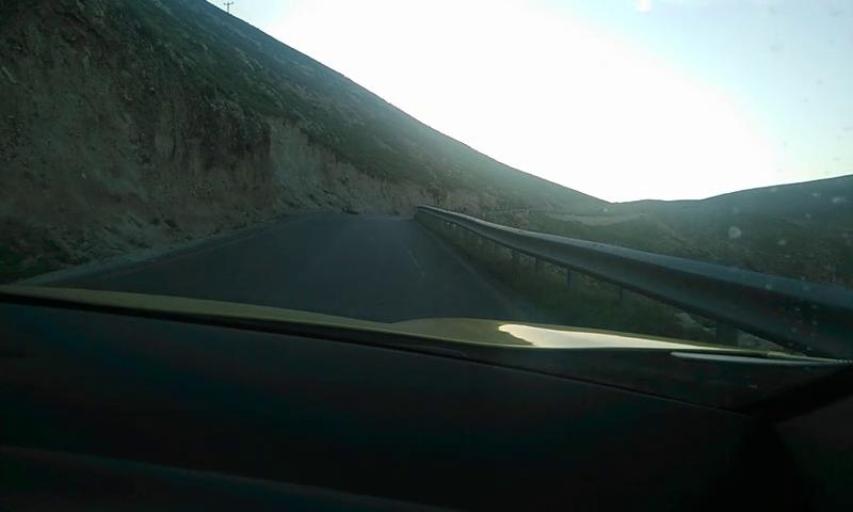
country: PS
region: West Bank
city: Rammun
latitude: 31.9107
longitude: 35.3655
